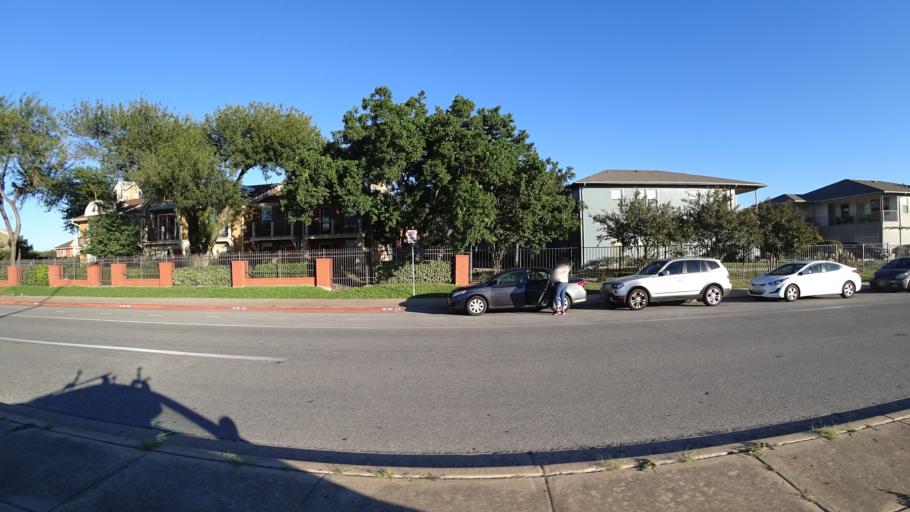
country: US
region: Texas
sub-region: Travis County
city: Austin
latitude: 30.2356
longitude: -97.7040
